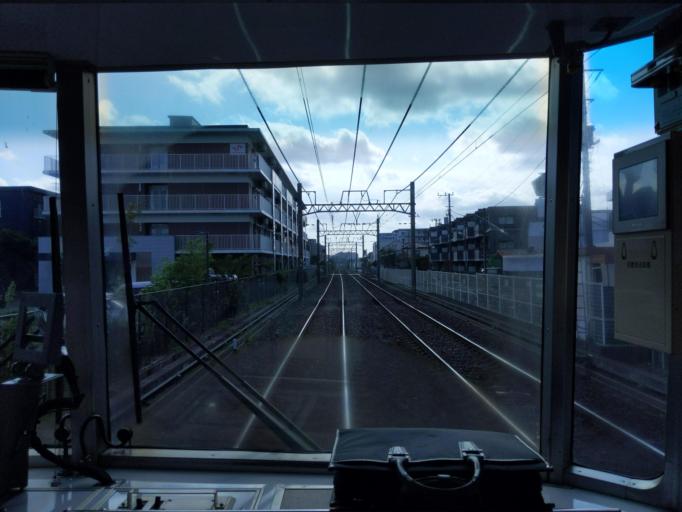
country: JP
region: Chiba
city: Funabashi
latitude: 35.7095
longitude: 140.0372
